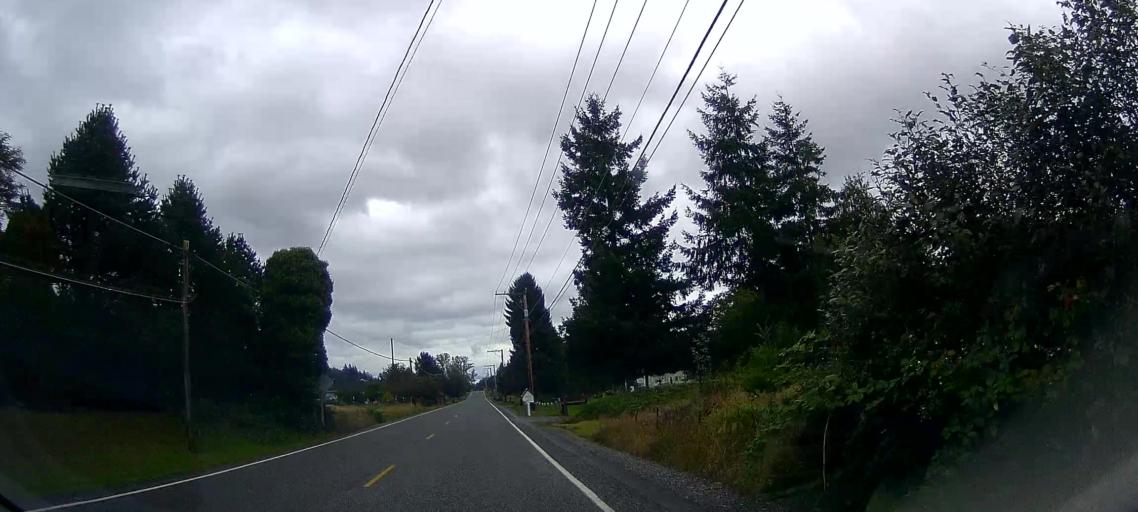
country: US
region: Washington
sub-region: Skagit County
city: Sedro-Woolley
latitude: 48.5266
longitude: -122.0831
